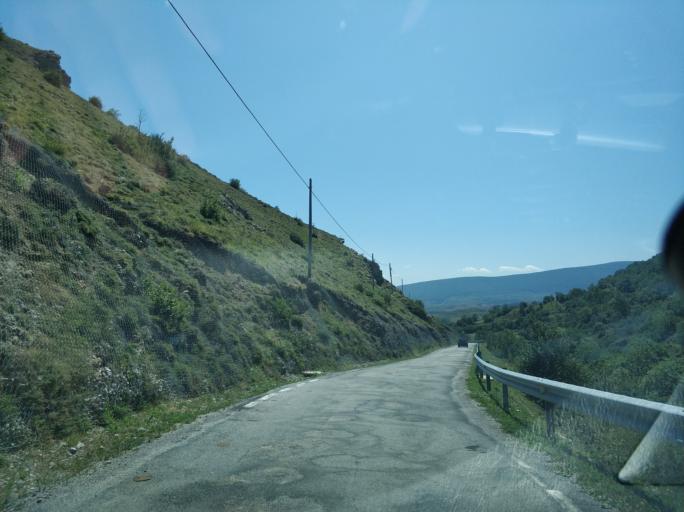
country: ES
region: Cantabria
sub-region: Provincia de Cantabria
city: Reinosa
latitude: 43.0281
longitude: -4.1688
